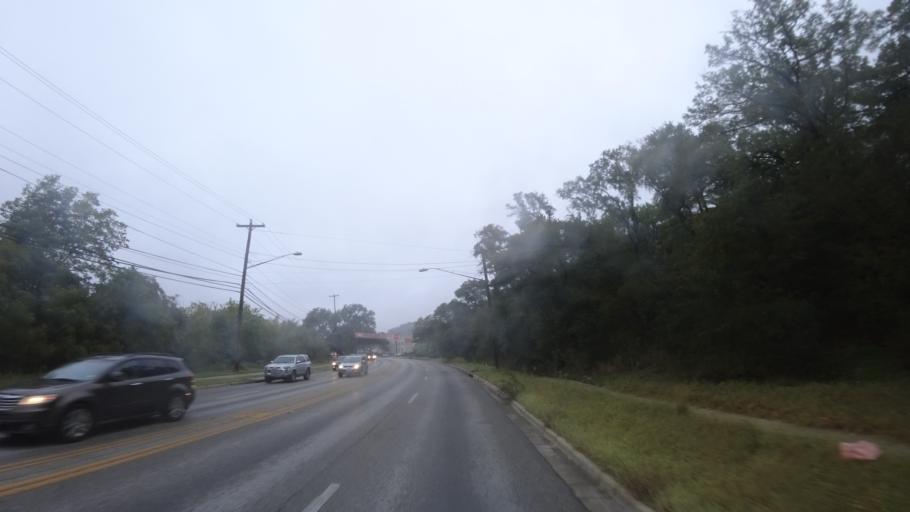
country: US
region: Texas
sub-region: Travis County
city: Austin
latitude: 30.2815
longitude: -97.7506
